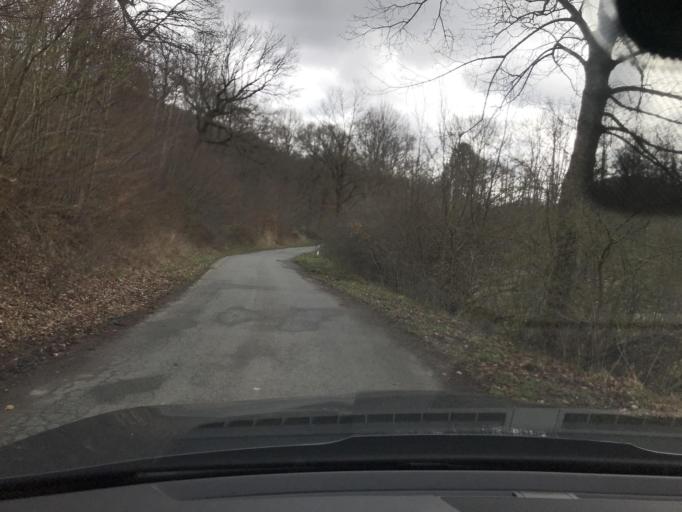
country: DE
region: Saxony-Anhalt
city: Harzgerode
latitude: 51.6756
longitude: 11.1875
